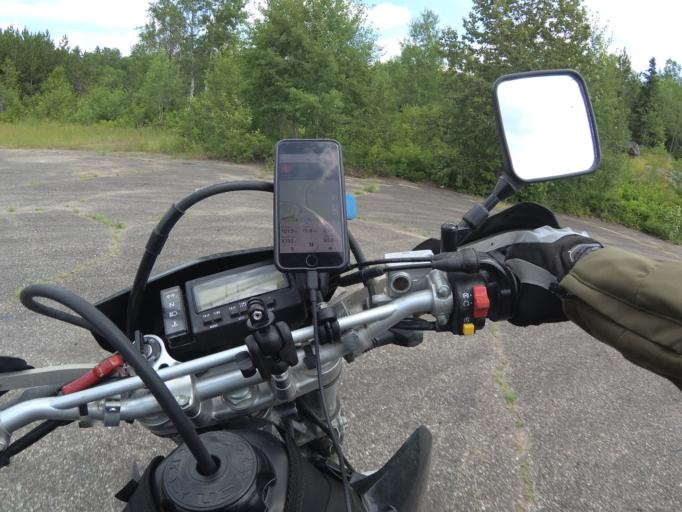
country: CA
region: Ontario
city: Bancroft
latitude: 45.0318
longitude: -77.2662
